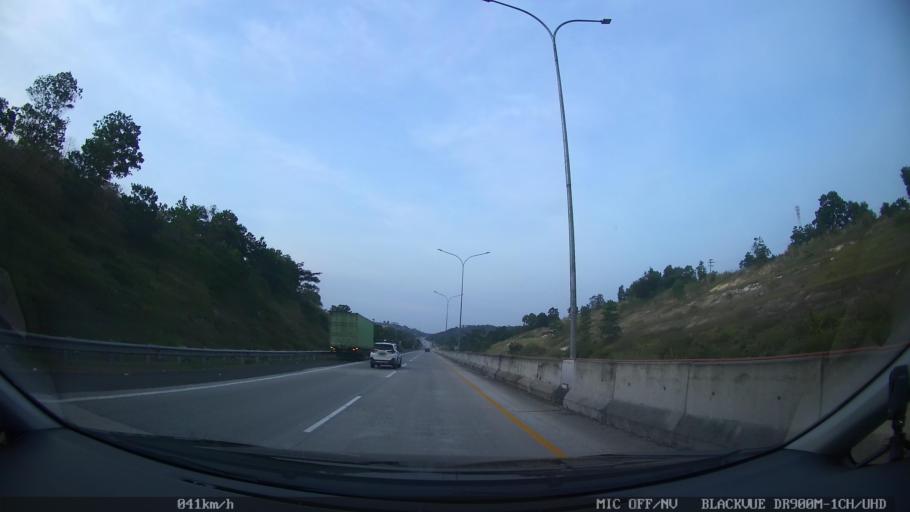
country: ID
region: Lampung
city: Penengahan
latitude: -5.8411
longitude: 105.7289
